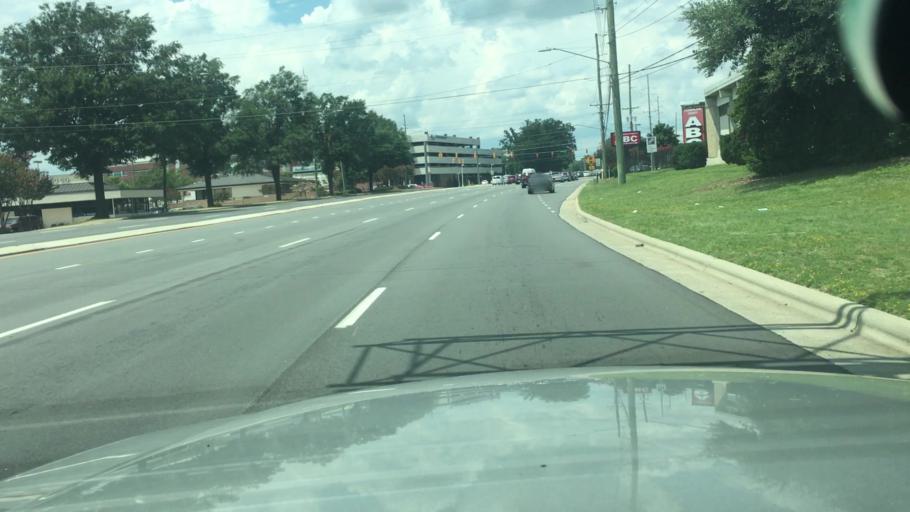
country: US
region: North Carolina
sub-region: Cumberland County
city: Fayetteville
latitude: 35.0291
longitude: -78.9291
